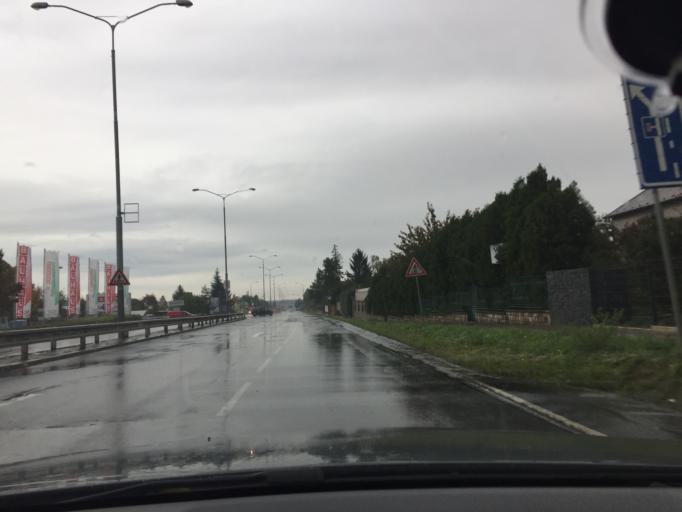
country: CZ
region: Central Bohemia
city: Zdiby
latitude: 50.1363
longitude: 14.4524
